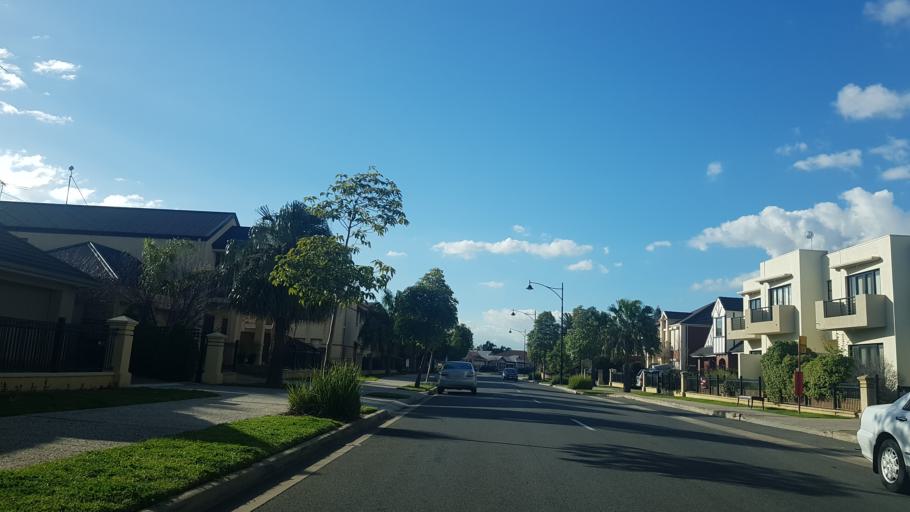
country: AU
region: South Australia
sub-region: Salisbury
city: Ingle Farm
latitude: -34.8145
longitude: 138.6078
